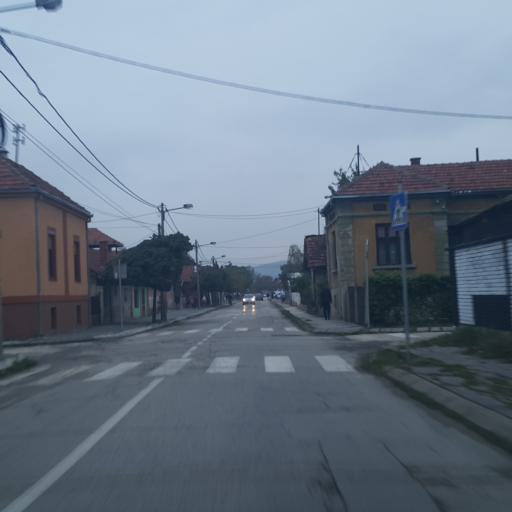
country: RS
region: Central Serbia
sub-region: Zajecarski Okrug
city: Zajecar
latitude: 43.9023
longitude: 22.2678
